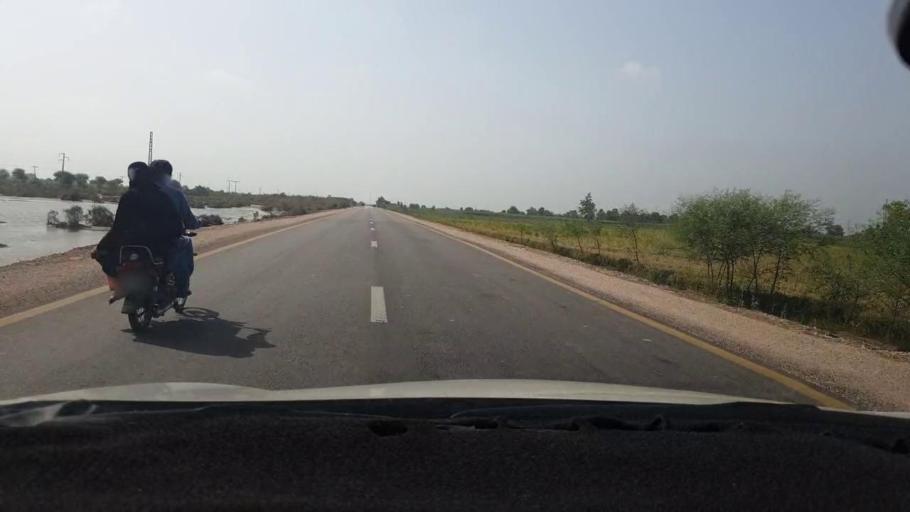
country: PK
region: Sindh
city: Jhol
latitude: 25.8542
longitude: 69.0601
